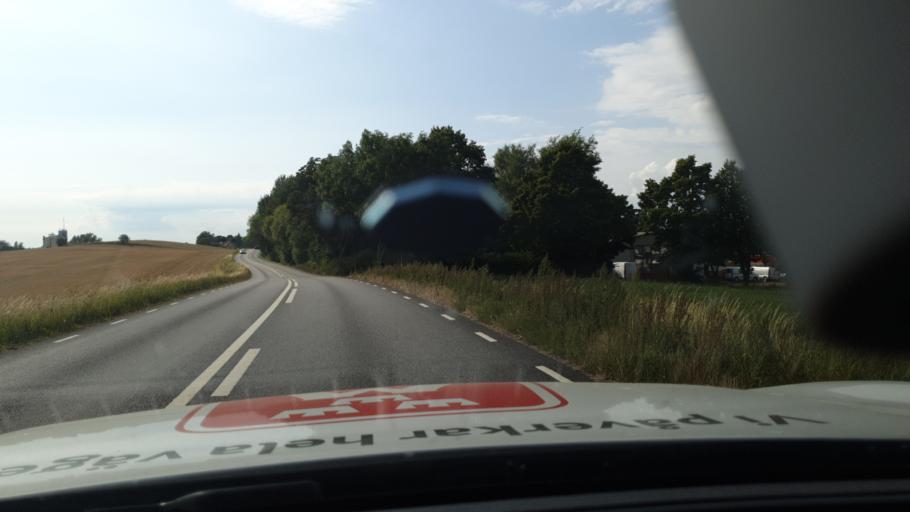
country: SE
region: Skane
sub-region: Svedala Kommun
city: Svedala
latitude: 55.4540
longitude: 13.2283
